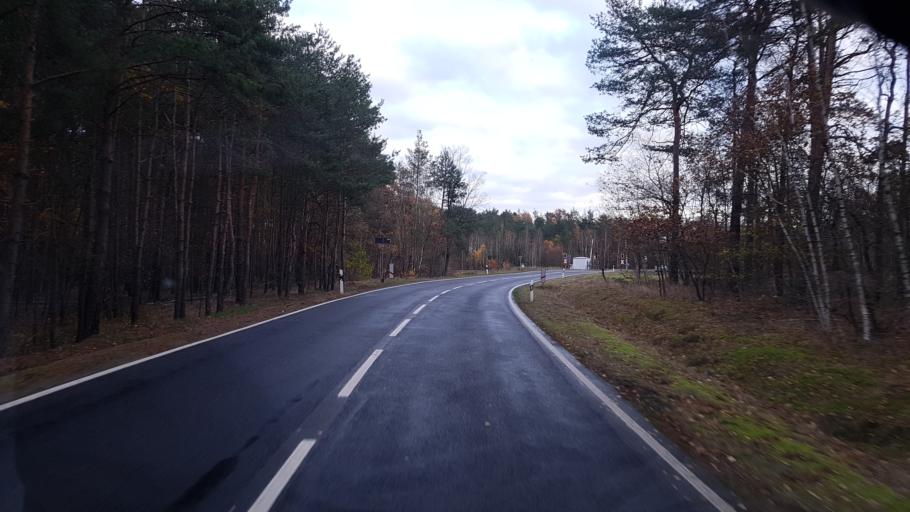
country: DE
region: Brandenburg
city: Ortrand
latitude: 51.3827
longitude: 13.7712
